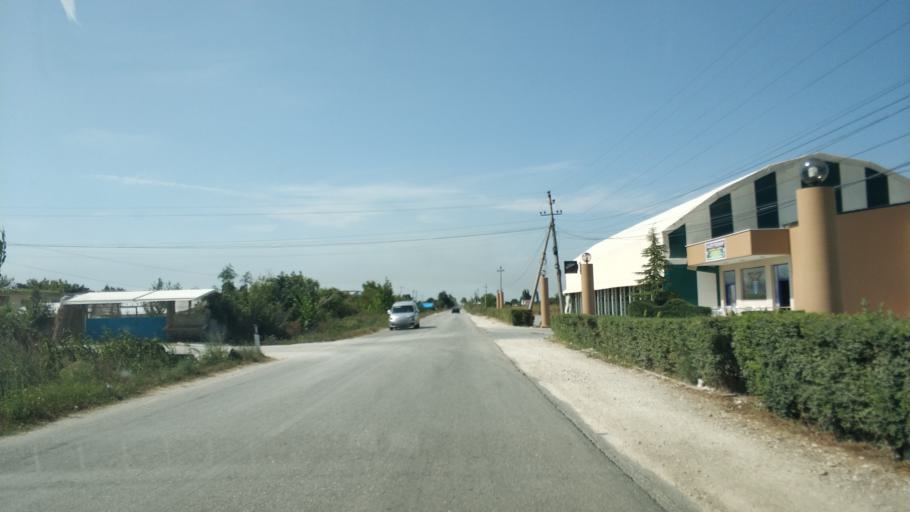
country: AL
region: Fier
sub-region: Rrethi i Fierit
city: Dermenas
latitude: 40.7381
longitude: 19.5165
